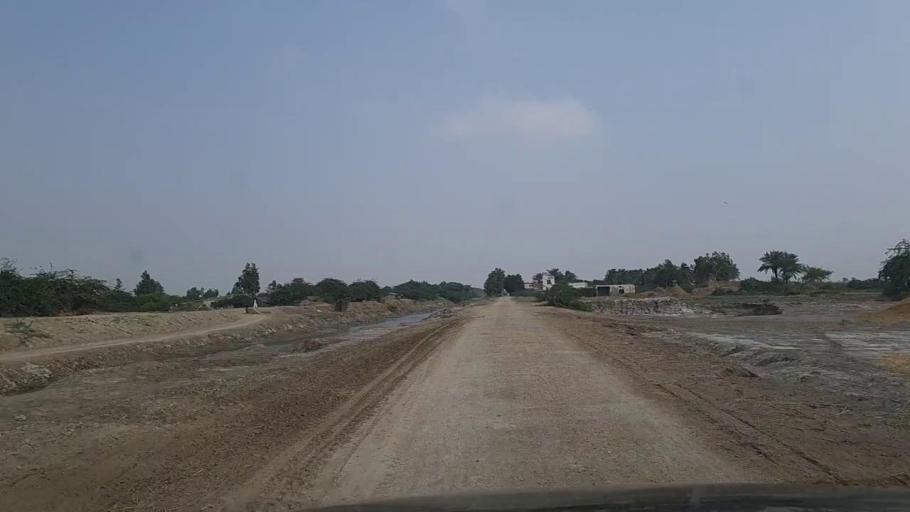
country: PK
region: Sindh
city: Thatta
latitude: 24.7789
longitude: 67.8358
